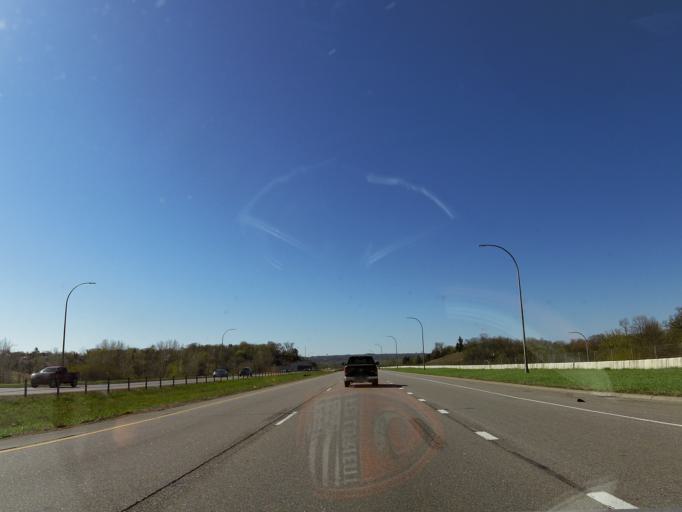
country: US
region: Minnesota
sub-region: Scott County
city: Savage
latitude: 44.8110
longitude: -93.3985
